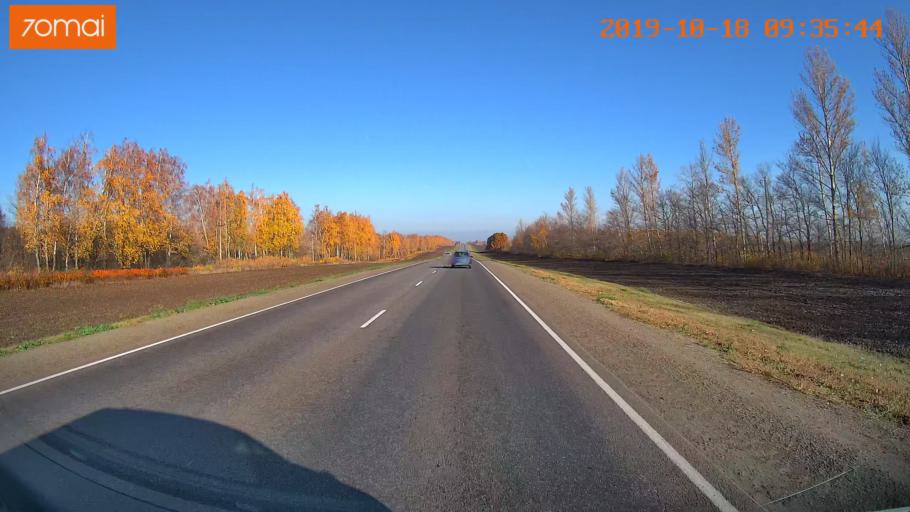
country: RU
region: Tula
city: Yefremov
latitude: 53.1962
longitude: 38.1476
